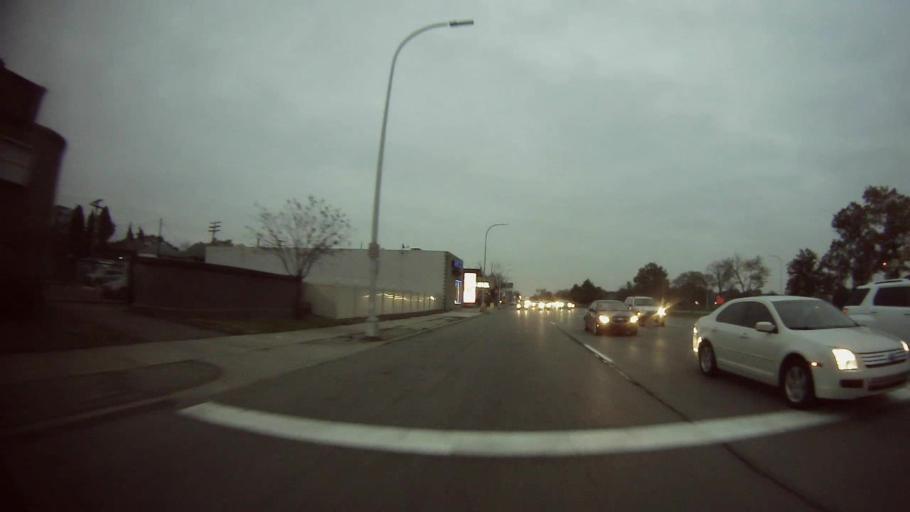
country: US
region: Michigan
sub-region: Wayne County
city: Highland Park
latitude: 42.4234
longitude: -83.1090
